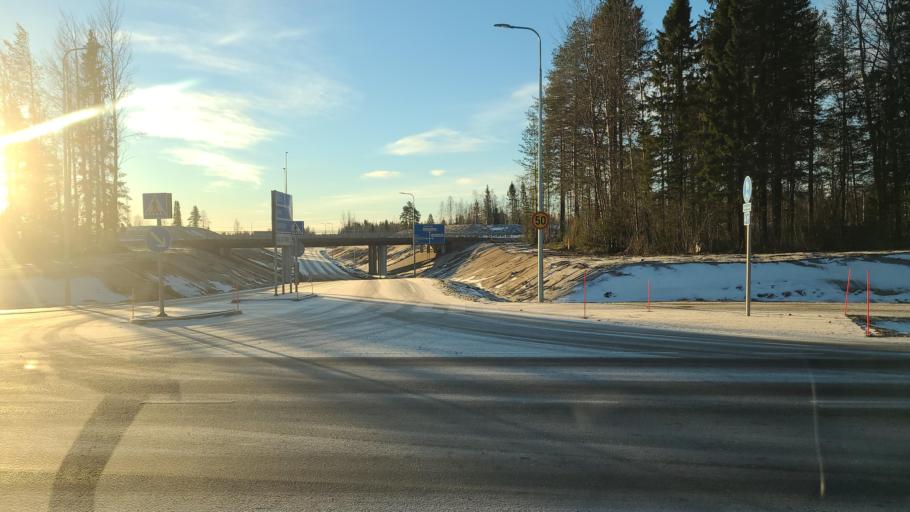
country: FI
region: Lapland
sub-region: Kemi-Tornio
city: Kemi
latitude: 65.6798
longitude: 24.7442
